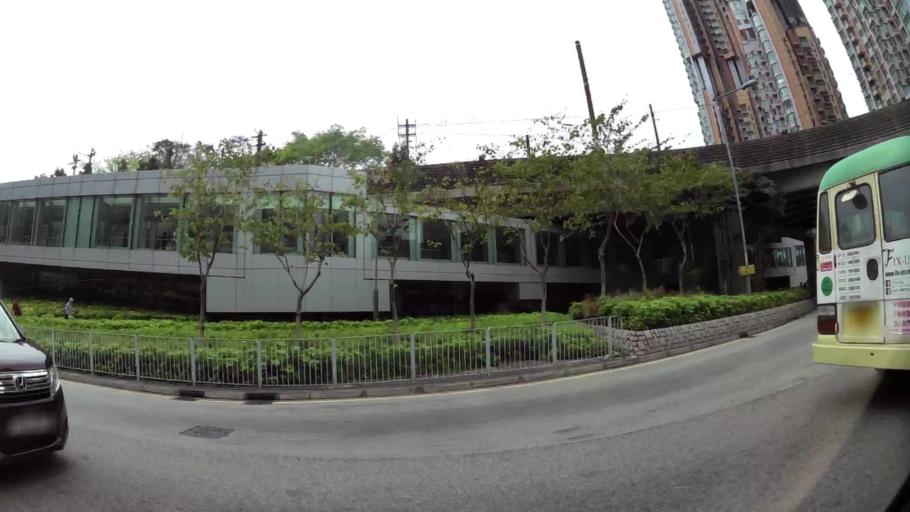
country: HK
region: Tuen Mun
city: Tuen Mun
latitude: 22.3938
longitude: 113.9749
